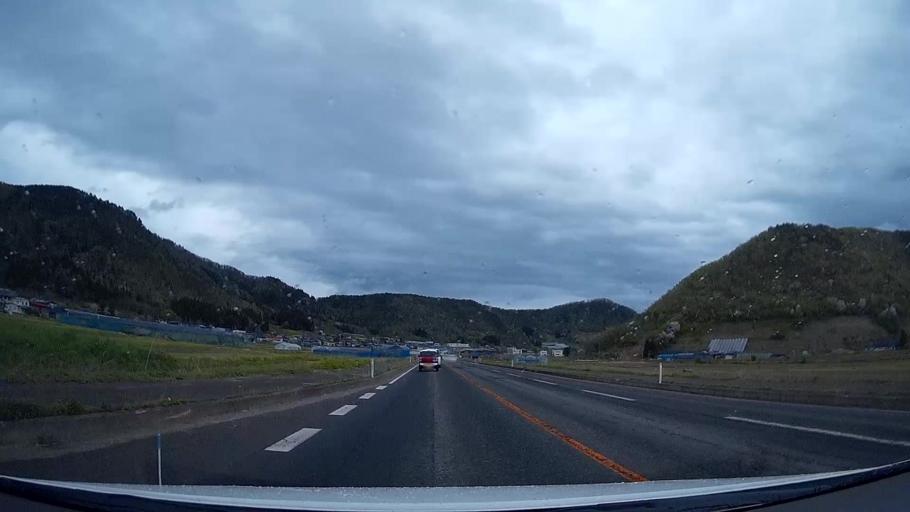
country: JP
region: Yamagata
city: Takahata
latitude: 38.0831
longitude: 140.1866
